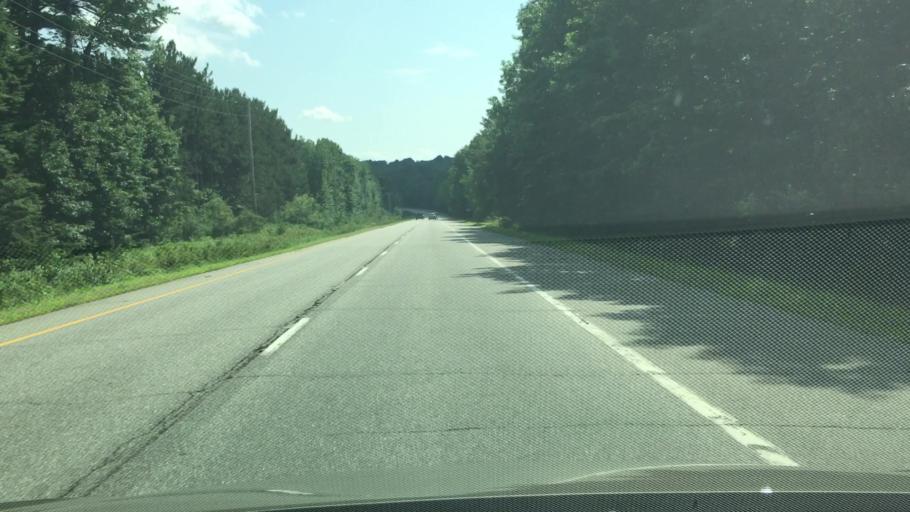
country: US
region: Maine
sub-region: Androscoggin County
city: Auburn
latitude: 44.0639
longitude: -70.2525
